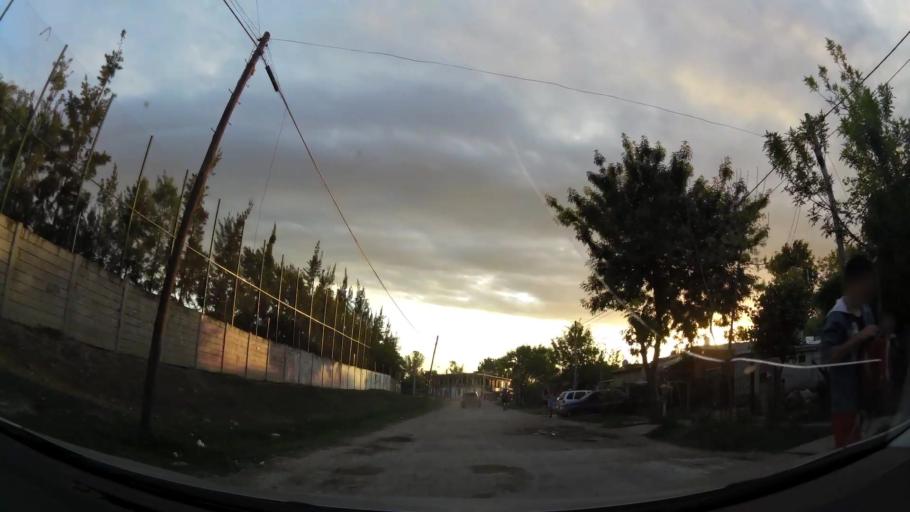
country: AR
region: Buenos Aires
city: Santa Catalina - Dique Lujan
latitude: -34.4373
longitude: -58.6662
